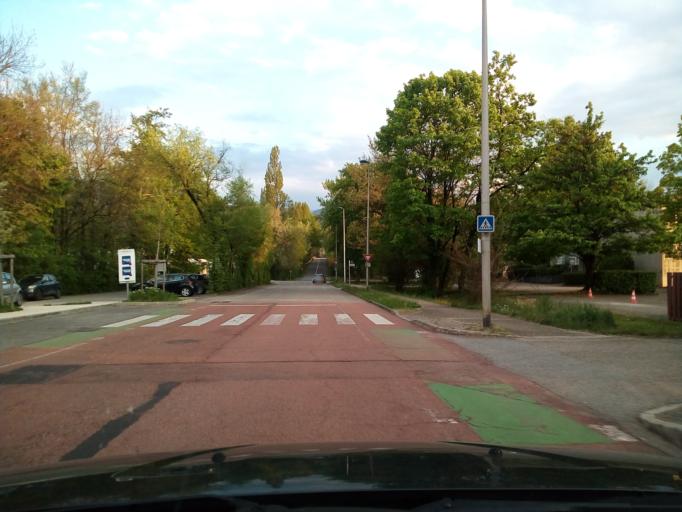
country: FR
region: Rhone-Alpes
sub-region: Departement de l'Isere
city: Meylan
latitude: 45.2084
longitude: 5.7879
